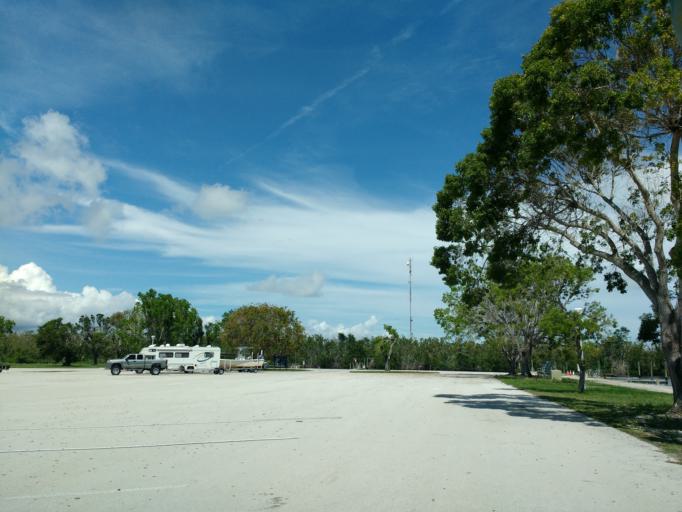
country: US
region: Florida
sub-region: Monroe County
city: Islamorada
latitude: 25.1437
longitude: -80.9238
